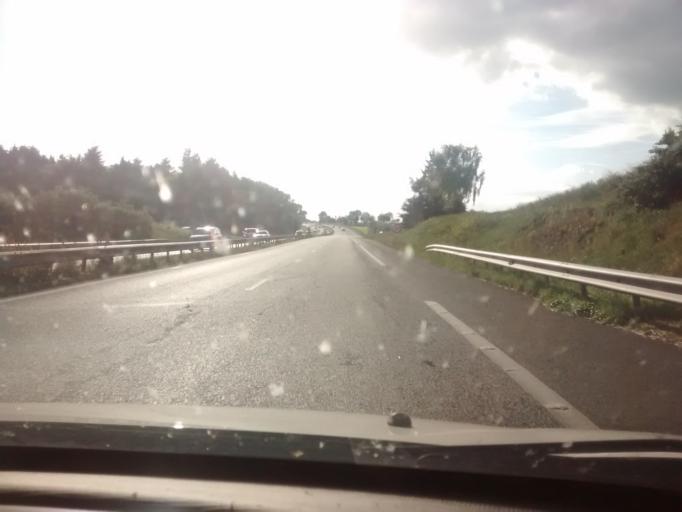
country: FR
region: Brittany
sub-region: Departement d'Ille-et-Vilaine
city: Noyal-sur-Vilaine
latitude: 48.1105
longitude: -1.5332
